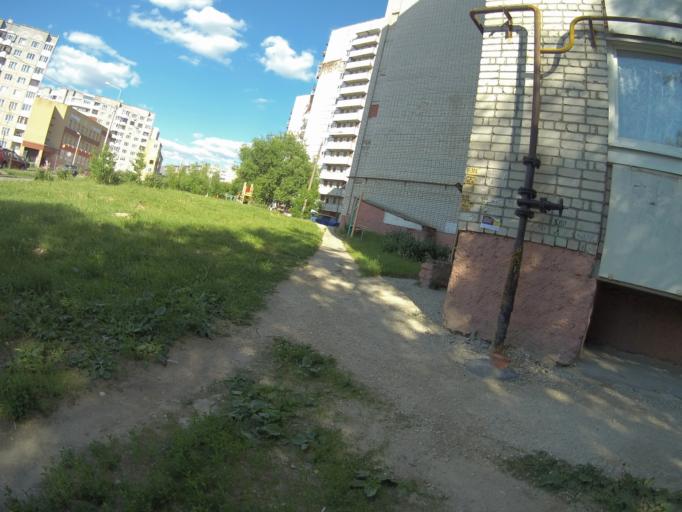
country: RU
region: Vladimir
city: Kommunar
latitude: 56.1612
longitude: 40.4607
